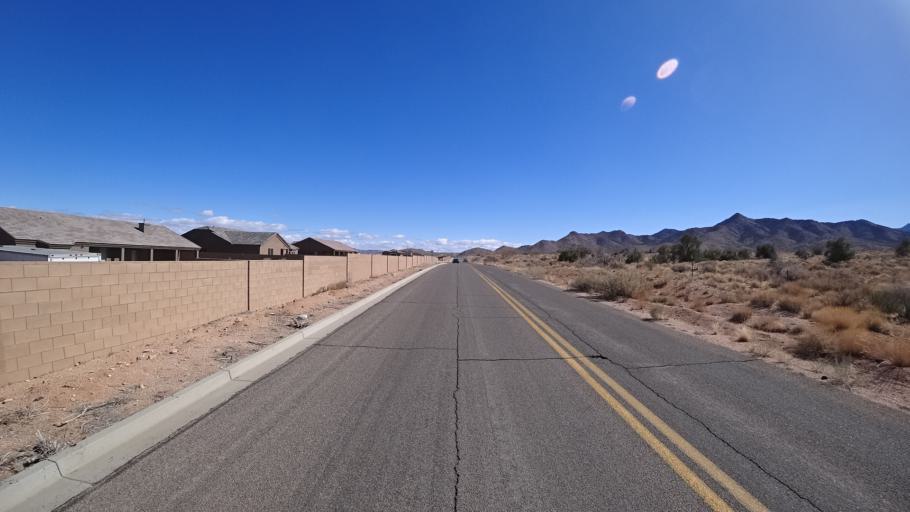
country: US
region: Arizona
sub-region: Mohave County
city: Kingman
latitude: 35.1960
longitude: -113.9668
